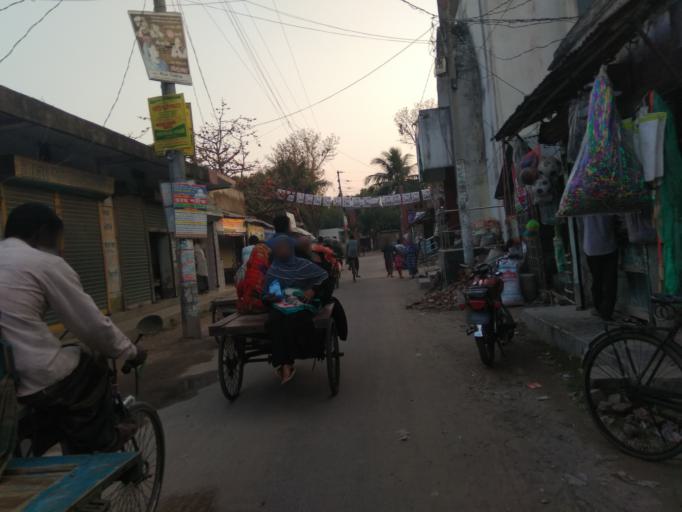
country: BD
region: Khulna
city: Satkhira
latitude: 22.5479
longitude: 89.1755
